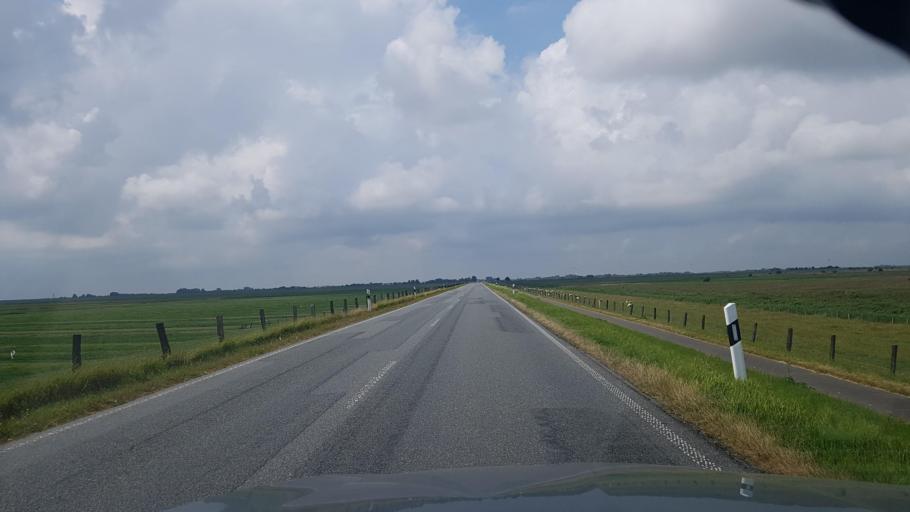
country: DE
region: Schleswig-Holstein
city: Wobbenbull
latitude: 54.5193
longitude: 8.9644
